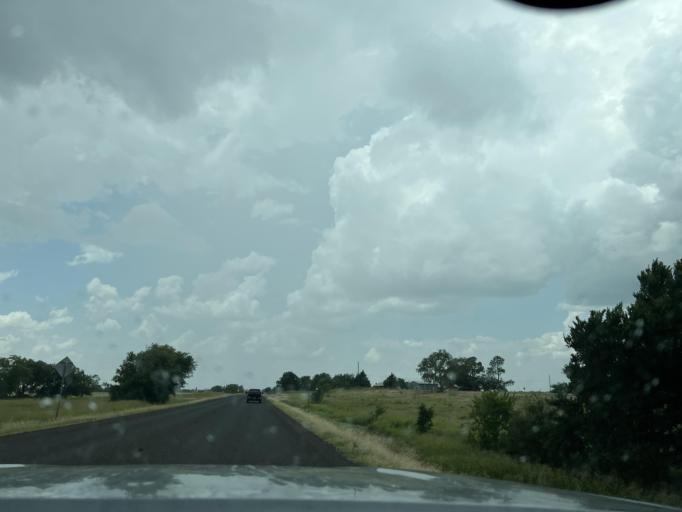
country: US
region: Texas
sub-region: Wise County
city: Boyd
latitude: 33.1475
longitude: -97.6374
